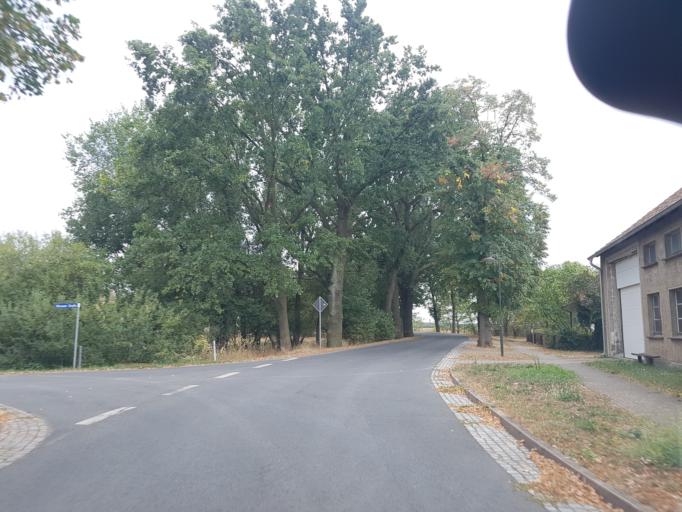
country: DE
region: Saxony-Anhalt
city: Annaburg
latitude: 51.7806
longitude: 13.0540
